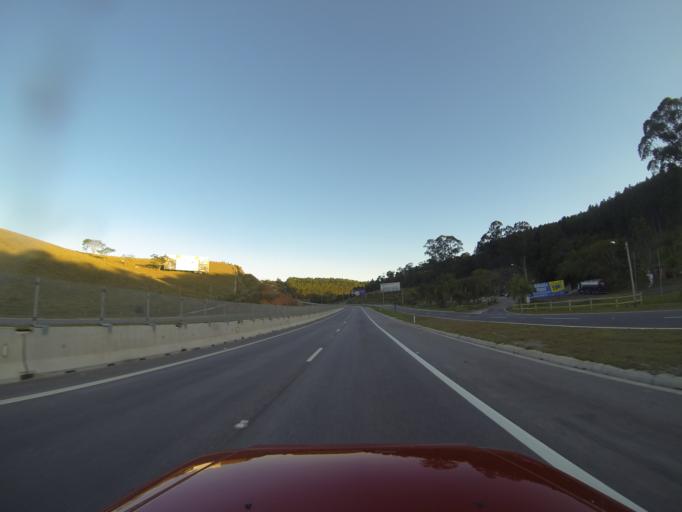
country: BR
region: Sao Paulo
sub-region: Caraguatatuba
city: Caraguatatuba
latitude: -23.4480
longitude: -45.6035
